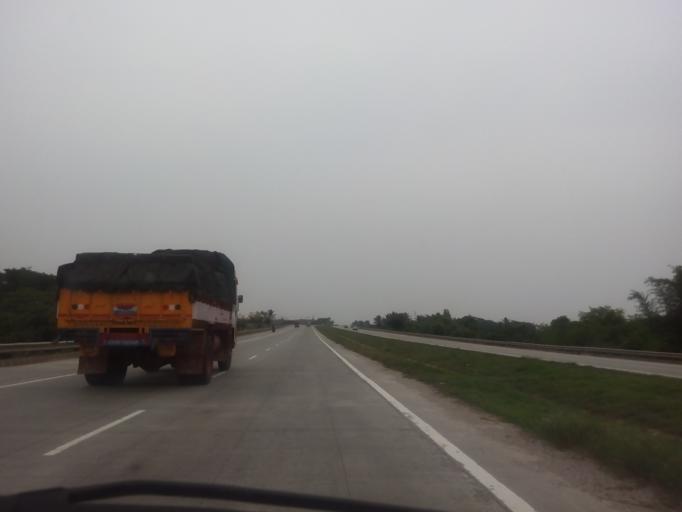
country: IN
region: Karnataka
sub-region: Bangalore Urban
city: Bangalore
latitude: 12.8917
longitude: 77.4810
